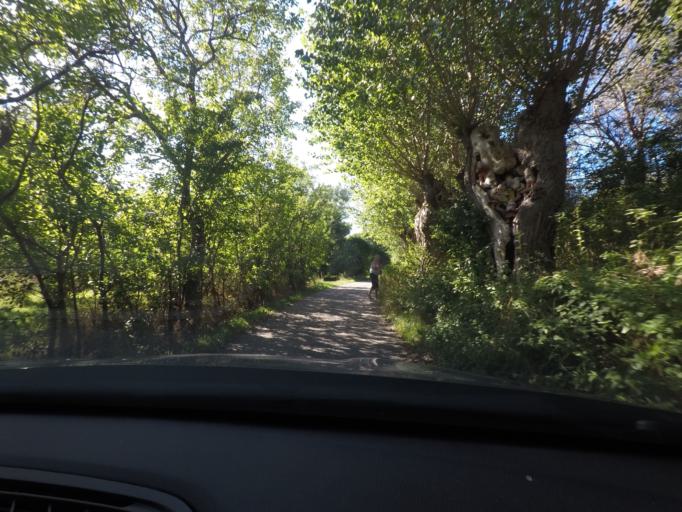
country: DK
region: Zealand
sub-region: Guldborgsund Kommune
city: Sakskobing
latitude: 54.9748
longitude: 11.5340
